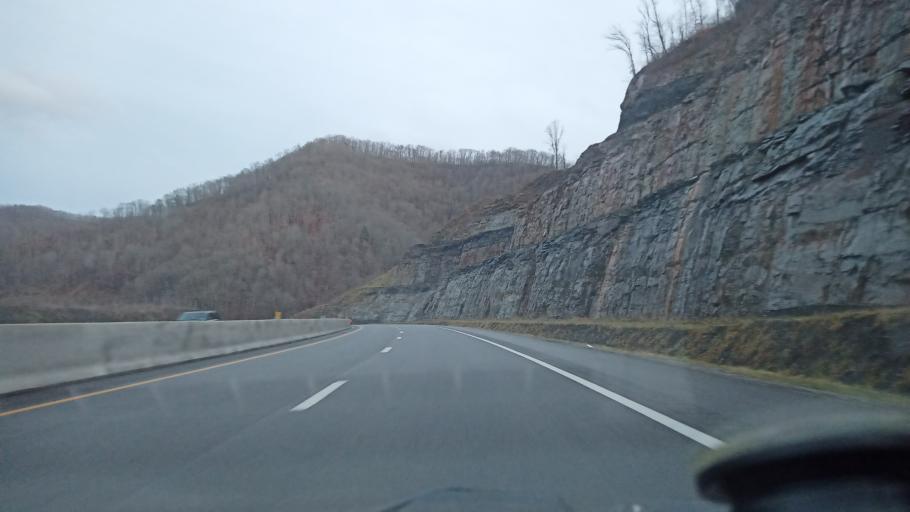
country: US
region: West Virginia
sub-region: Logan County
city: Logan
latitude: 37.8230
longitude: -81.9699
